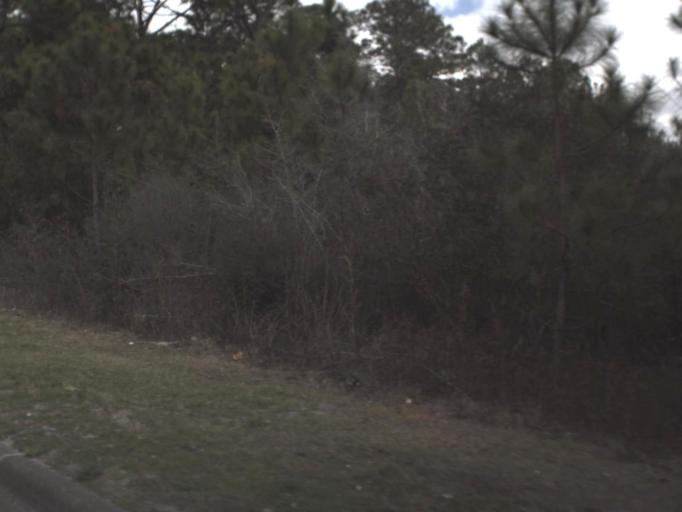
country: US
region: Florida
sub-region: Bay County
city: Springfield
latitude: 30.1690
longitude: -85.5910
